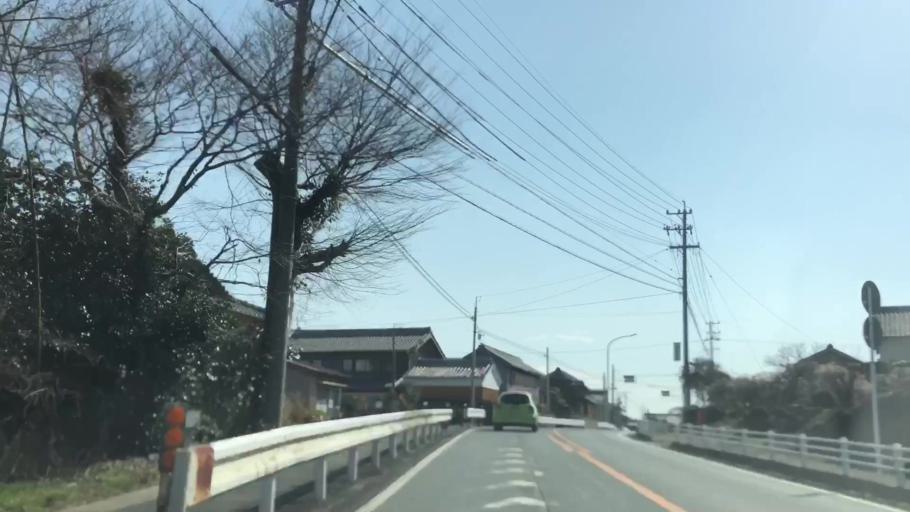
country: JP
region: Aichi
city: Tahara
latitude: 34.6863
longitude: 137.2810
